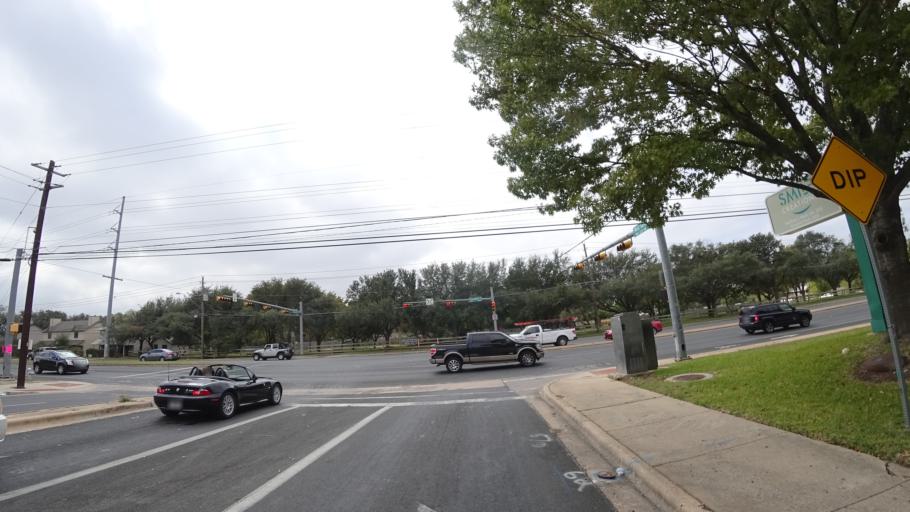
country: US
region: Texas
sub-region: Travis County
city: Shady Hollow
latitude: 30.1795
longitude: -97.8409
